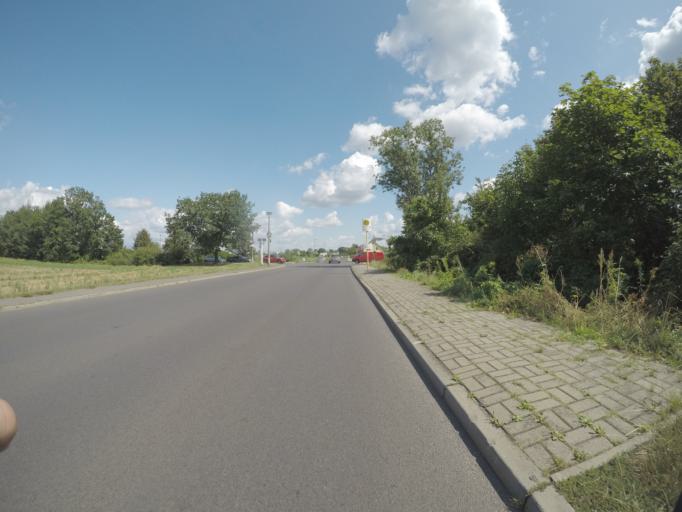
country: DE
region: Berlin
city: Kaulsdorf
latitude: 52.5024
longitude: 13.5968
